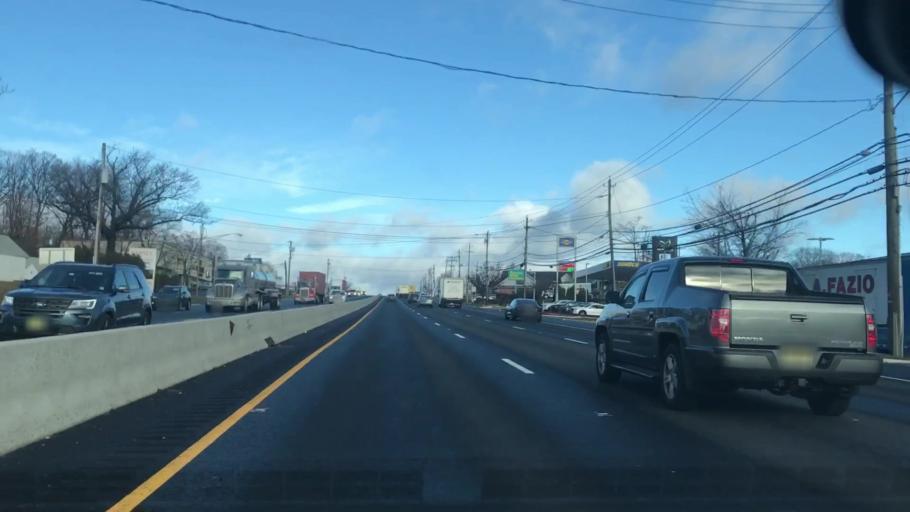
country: US
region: New Jersey
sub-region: Bergen County
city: Allendale
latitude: 41.0538
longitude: -74.1196
